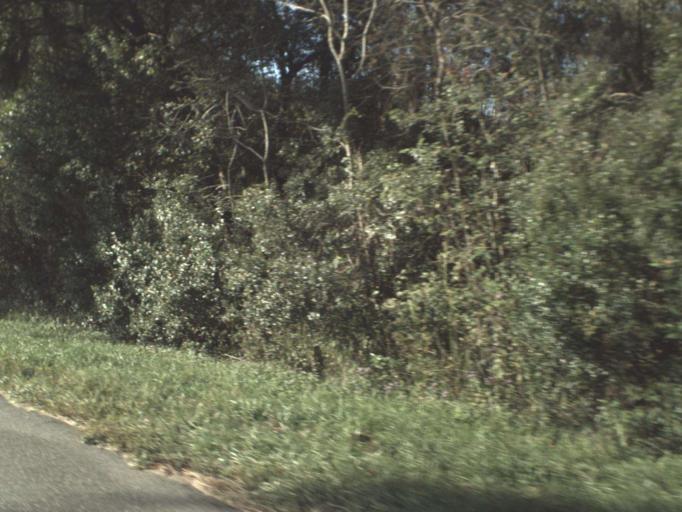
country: US
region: Georgia
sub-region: Brooks County
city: Quitman
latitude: 30.5795
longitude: -83.6370
